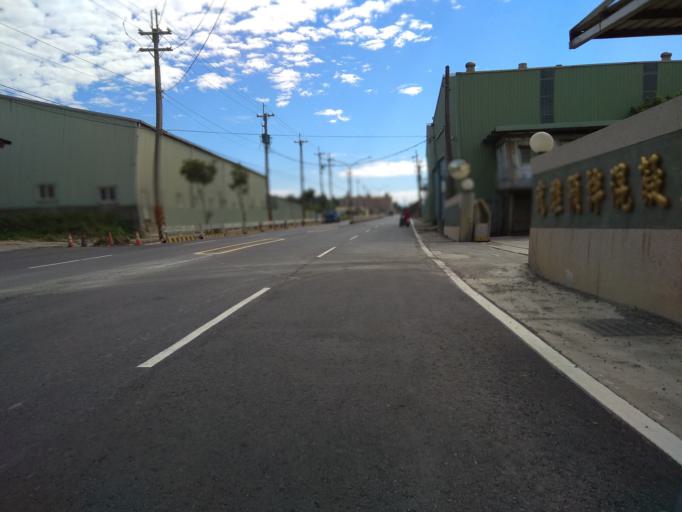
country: TW
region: Taiwan
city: Taoyuan City
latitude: 25.0616
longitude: 121.1338
